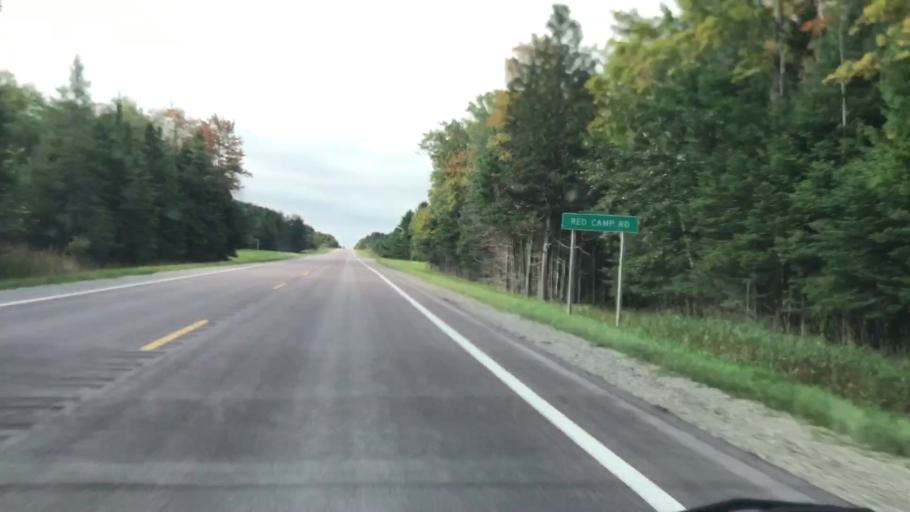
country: US
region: Michigan
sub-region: Luce County
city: Newberry
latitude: 46.2905
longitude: -85.5698
